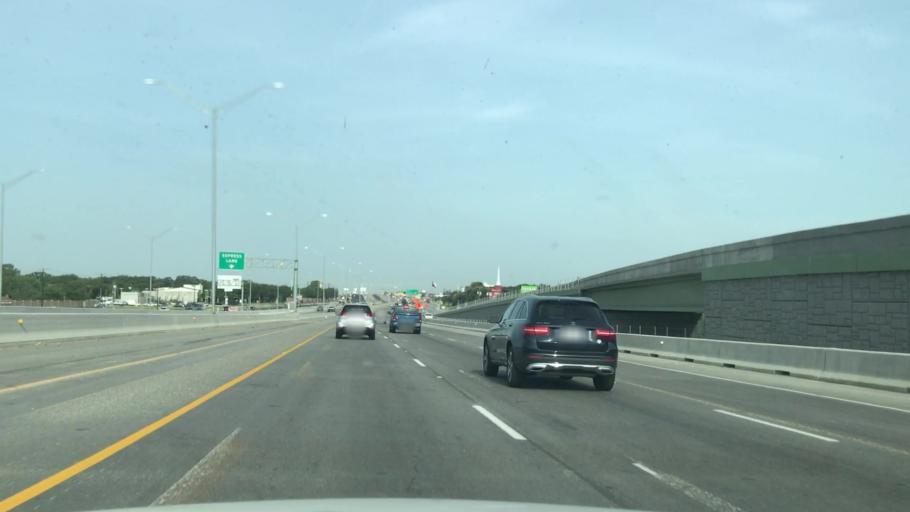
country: US
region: Texas
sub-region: Dallas County
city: Irving
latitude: 32.8375
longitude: -96.9616
